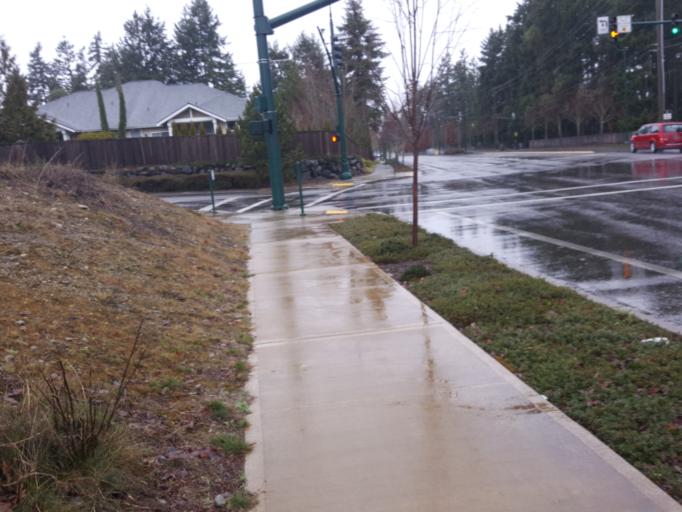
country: US
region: Washington
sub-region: Pierce County
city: University Place
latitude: 47.2078
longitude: -122.5347
